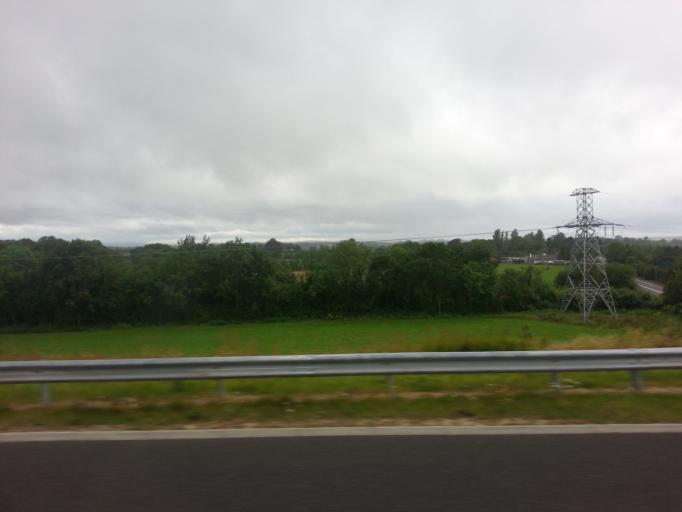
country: IE
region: Leinster
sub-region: Kilkenny
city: Kilkenny
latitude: 52.6404
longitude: -7.1688
